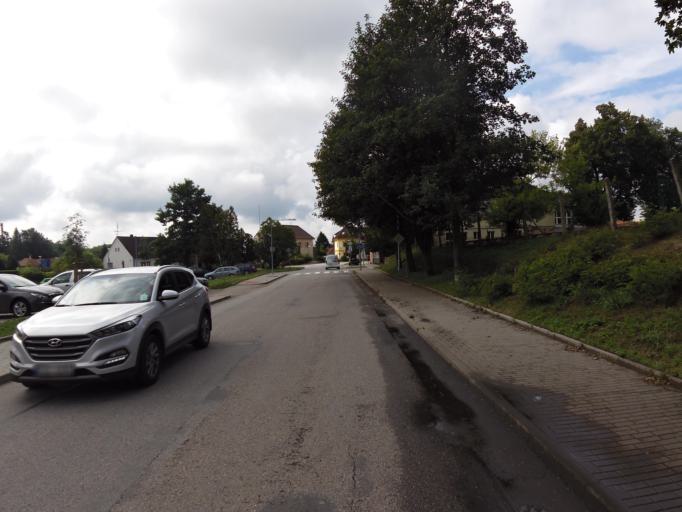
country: CZ
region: Jihocesky
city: Suchdol nad Luznici
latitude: 48.8923
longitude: 14.8795
